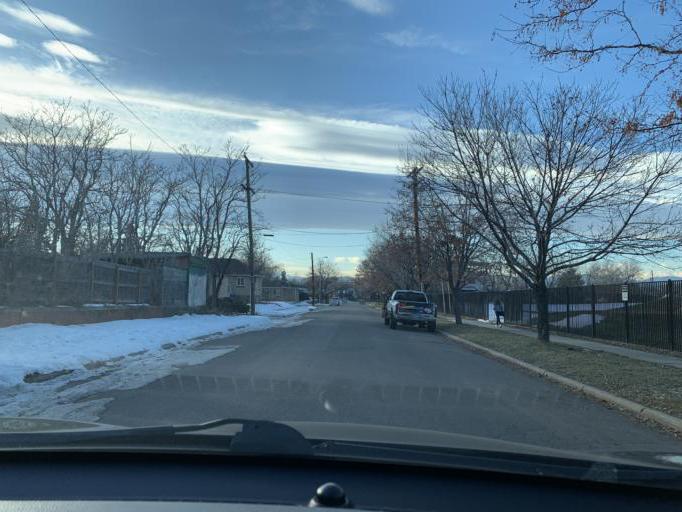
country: US
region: Colorado
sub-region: Adams County
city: Berkley
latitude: 39.7731
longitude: -105.0360
